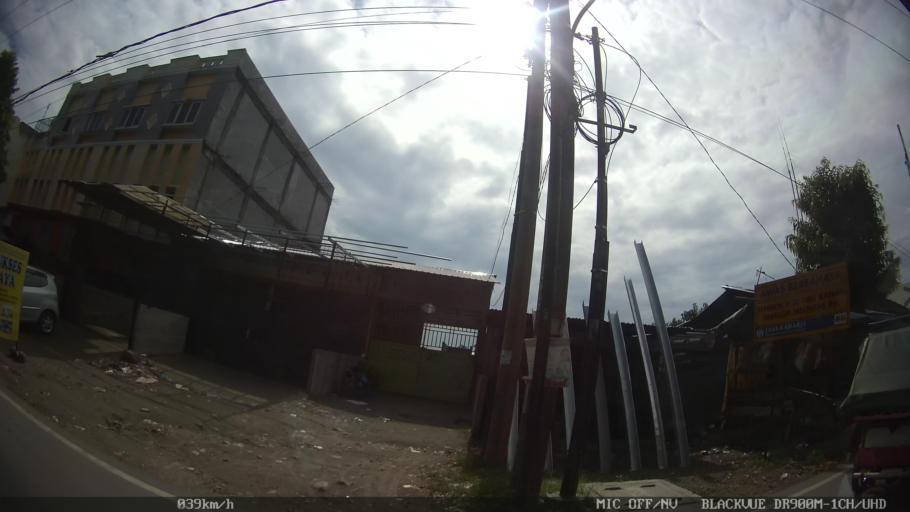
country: ID
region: North Sumatra
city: Sunggal
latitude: 3.6055
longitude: 98.6083
